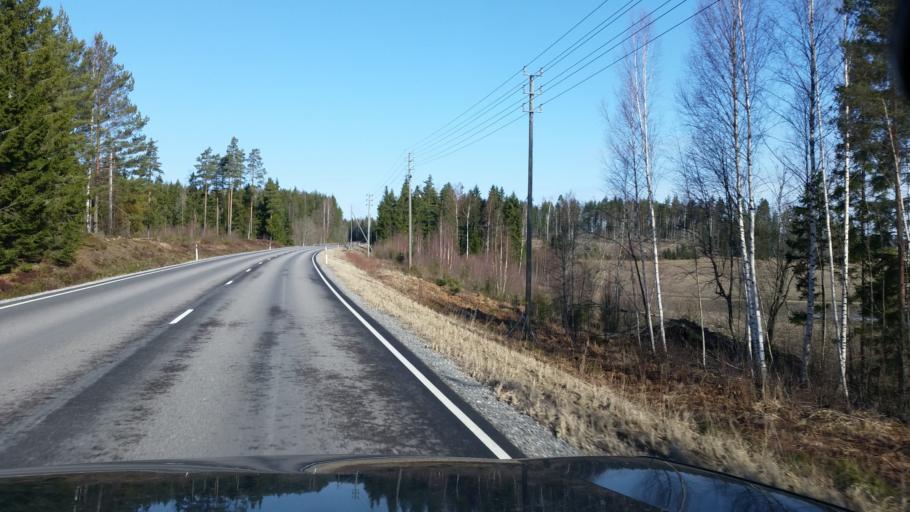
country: FI
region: Uusimaa
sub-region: Raaseporin
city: Inga
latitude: 60.0802
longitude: 23.9496
